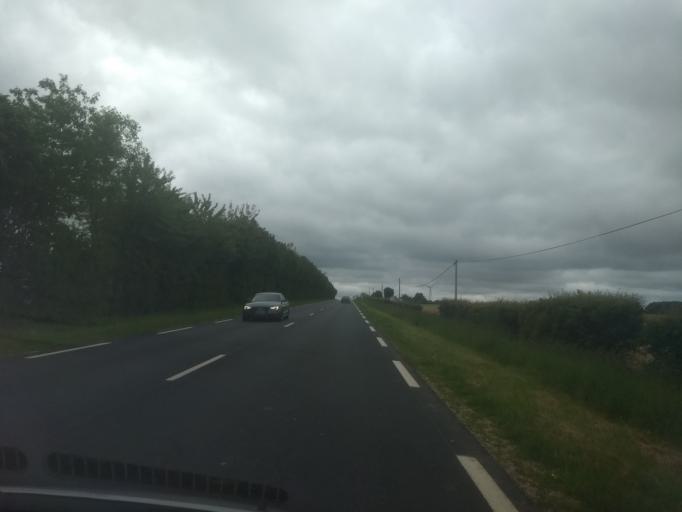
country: FR
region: Centre
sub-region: Departement d'Eure-et-Loir
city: Chateauneuf-en-Thymerais
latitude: 48.5708
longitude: 1.2256
